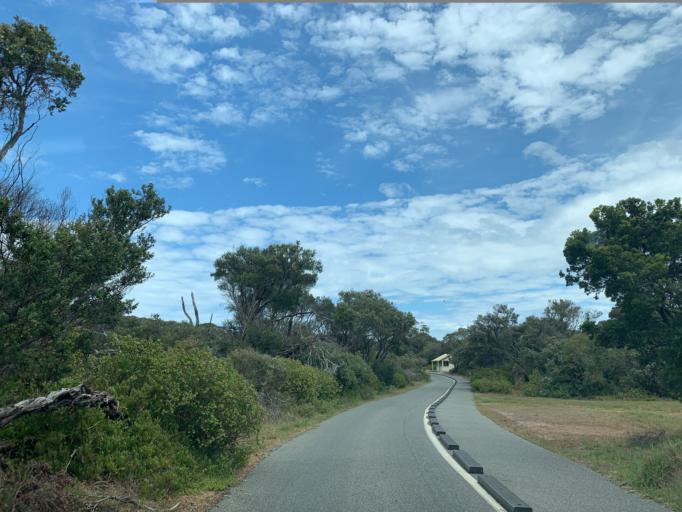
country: AU
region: Victoria
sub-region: Mornington Peninsula
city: Sorrento
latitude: -38.3151
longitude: 144.6927
